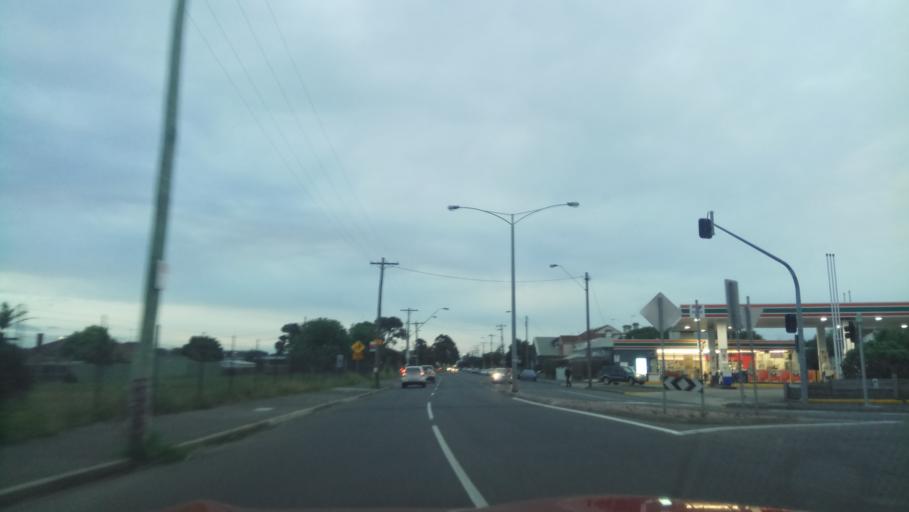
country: AU
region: Victoria
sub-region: Hobsons Bay
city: Williamstown North
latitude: -37.8578
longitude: 144.8885
